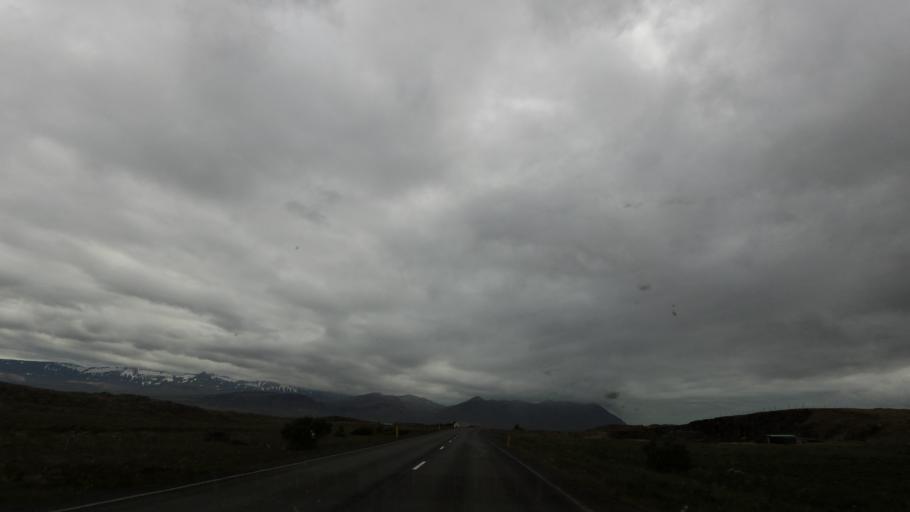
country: IS
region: West
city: Borgarnes
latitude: 64.6030
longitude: -21.8250
